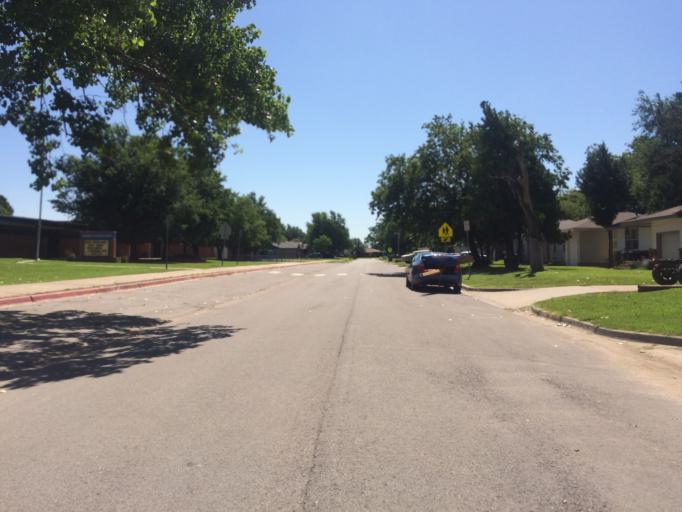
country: US
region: Oklahoma
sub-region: Cleveland County
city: Norman
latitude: 35.2279
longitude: -97.4577
